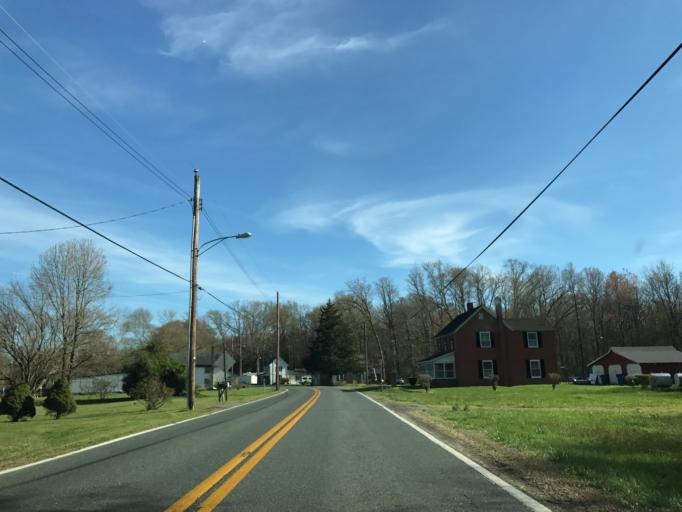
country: US
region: Maryland
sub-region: Caroline County
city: Greensboro
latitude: 39.0386
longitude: -75.7894
